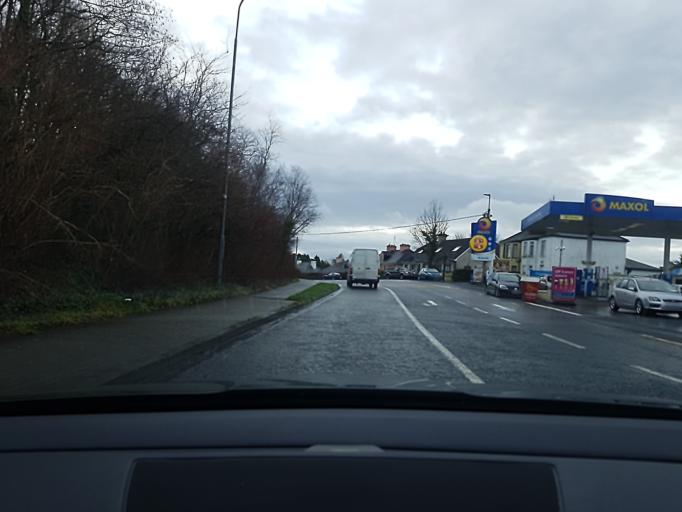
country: IE
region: Connaught
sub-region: Maigh Eo
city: Castlebar
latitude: 53.8515
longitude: -9.2928
